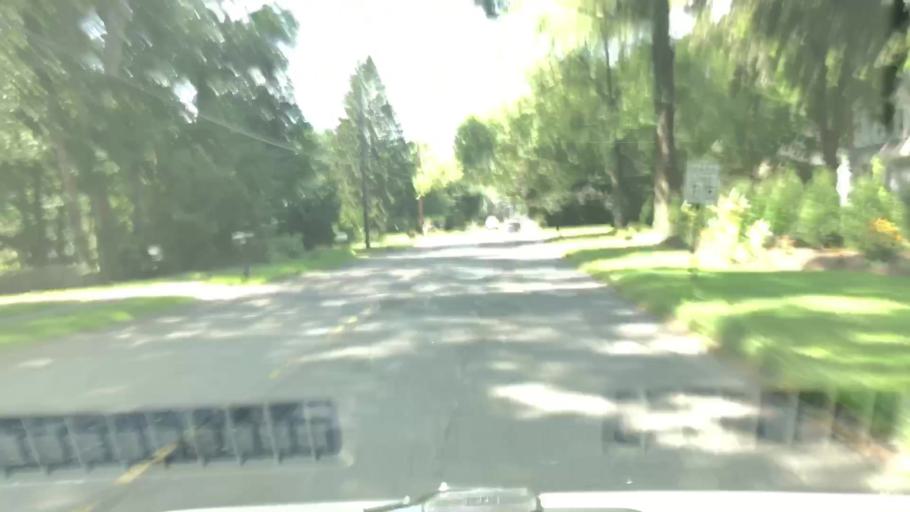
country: US
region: Massachusetts
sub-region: Hampshire County
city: Northampton
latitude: 42.3414
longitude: -72.6614
